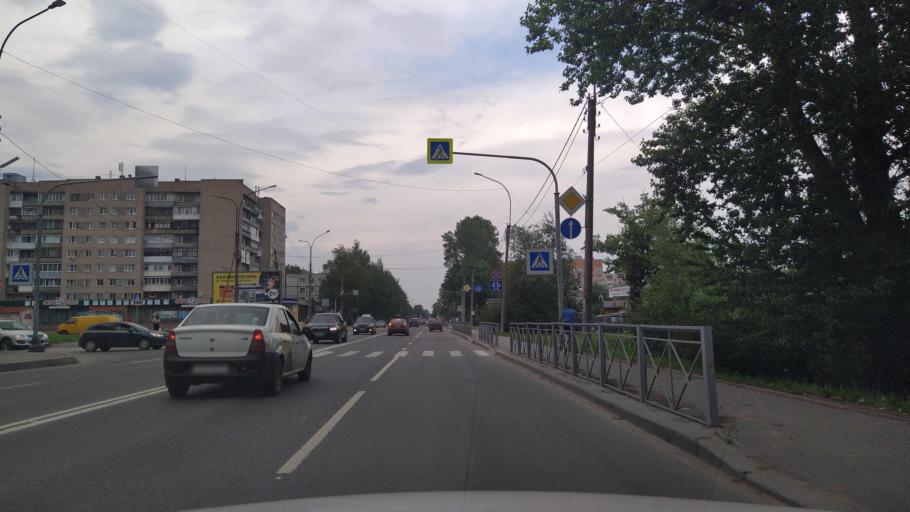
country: RU
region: Novgorod
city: Velikiy Novgorod
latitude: 58.5123
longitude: 31.2394
